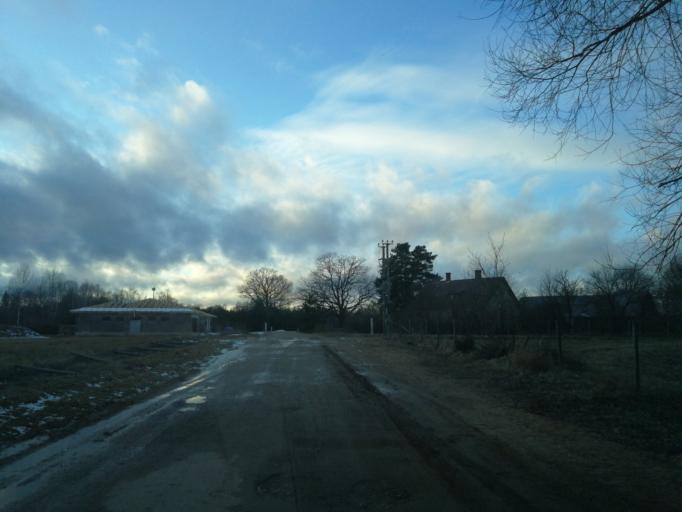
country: LV
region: Adazi
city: Adazi
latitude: 57.0734
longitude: 24.3509
